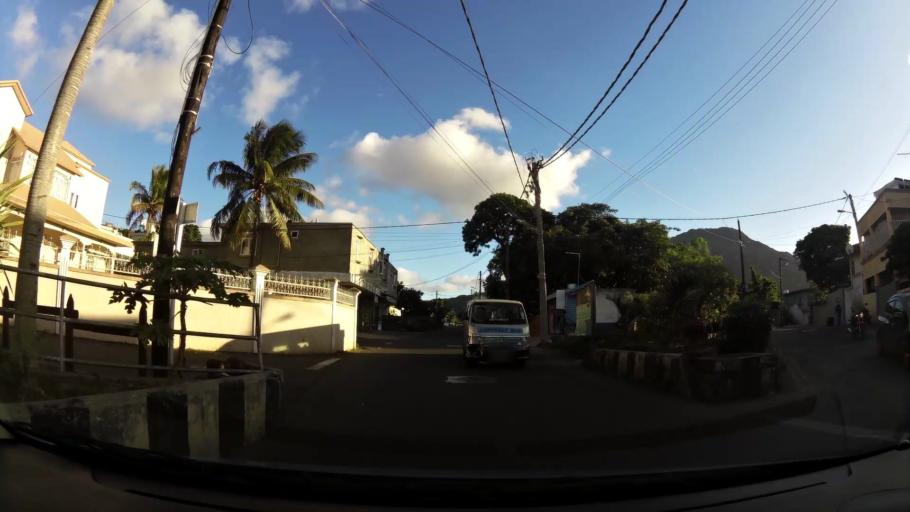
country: MU
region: Plaines Wilhems
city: Quatre Bornes
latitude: -20.2551
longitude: 57.4701
